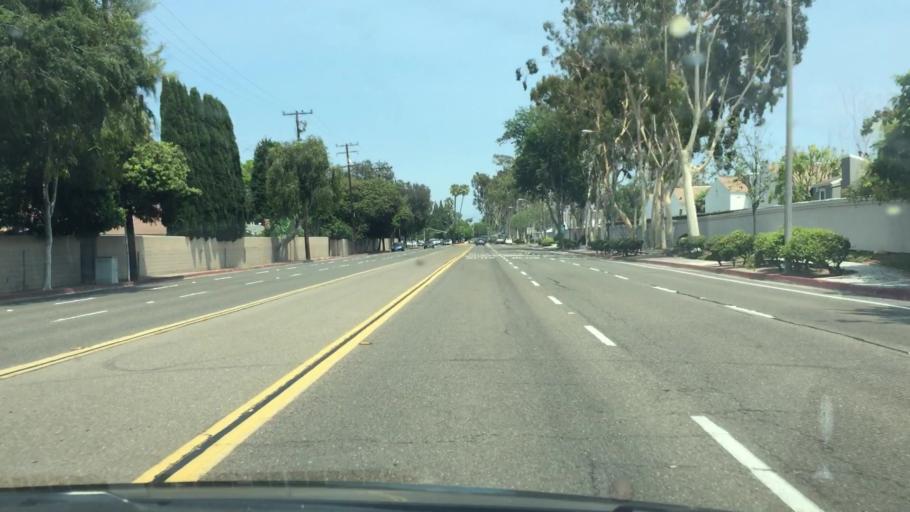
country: US
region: California
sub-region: Orange County
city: Costa Mesa
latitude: 33.6726
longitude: -117.9293
